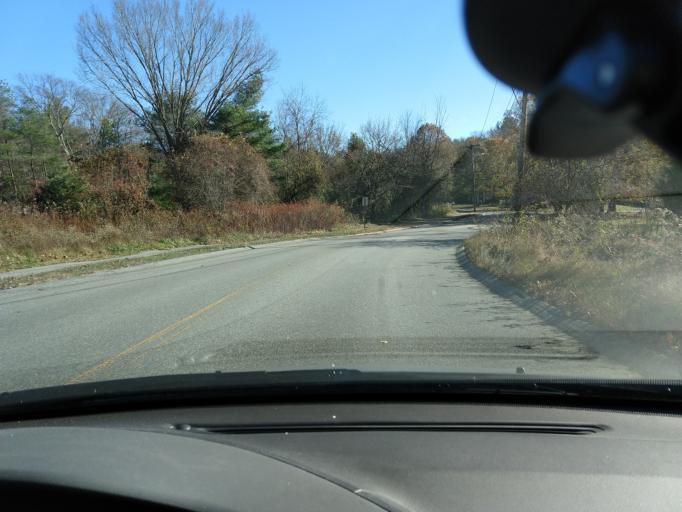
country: US
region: Massachusetts
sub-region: Middlesex County
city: Bedford
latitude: 42.5141
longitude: -71.2647
